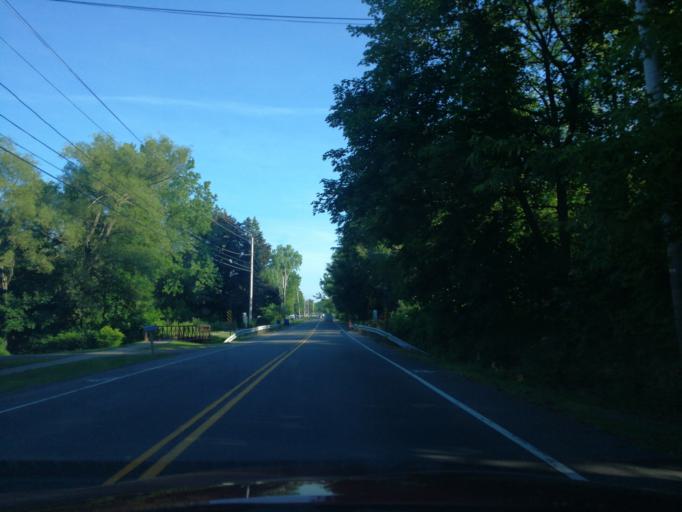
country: US
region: New York
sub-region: Monroe County
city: Greece
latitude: 43.2564
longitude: -77.7155
